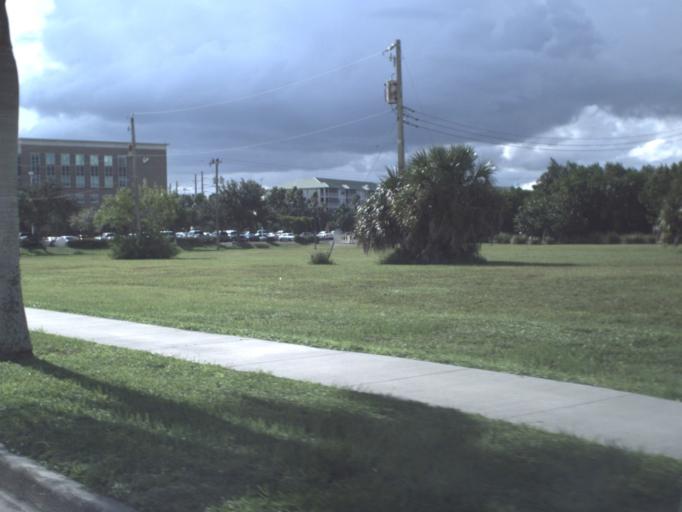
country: US
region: Florida
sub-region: Charlotte County
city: Punta Gorda
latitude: 26.9390
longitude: -82.0450
